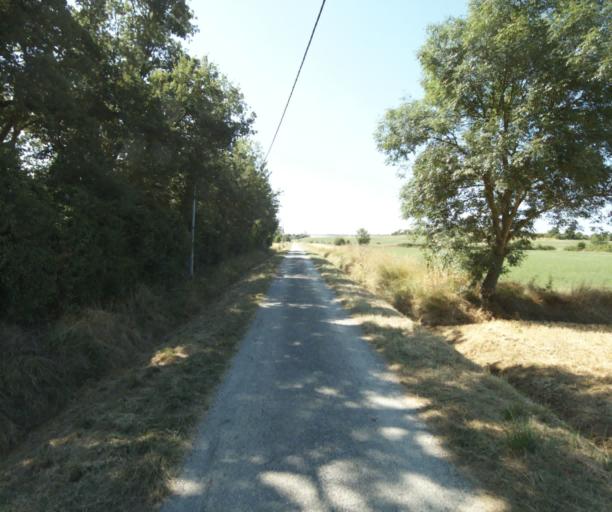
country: FR
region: Midi-Pyrenees
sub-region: Departement de la Haute-Garonne
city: Saint-Felix-Lauragais
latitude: 43.4739
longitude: 1.9061
